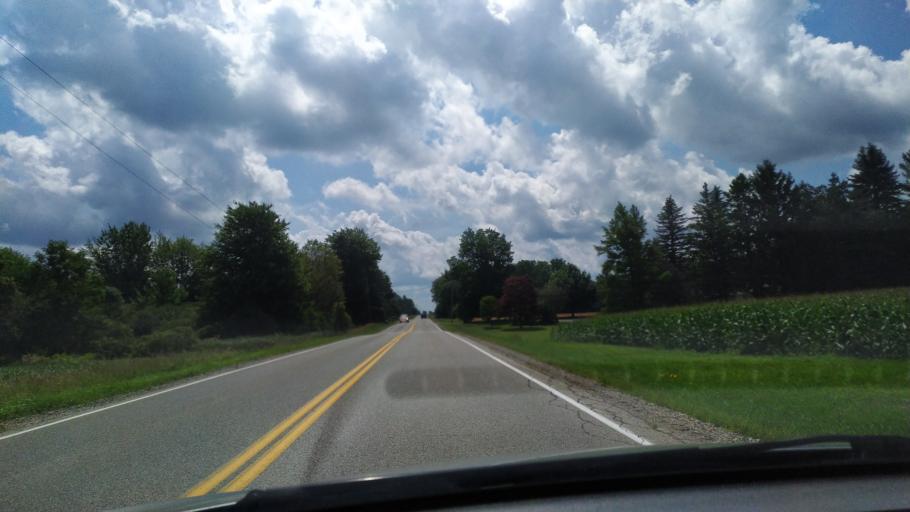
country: CA
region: Ontario
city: London
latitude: 43.0493
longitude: -81.3265
